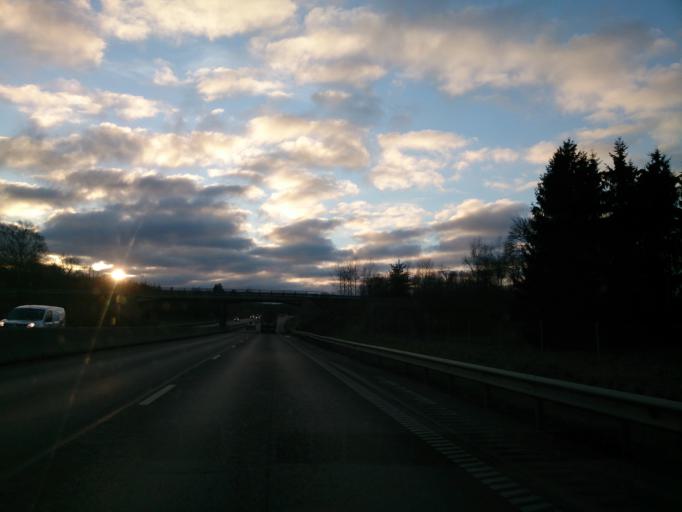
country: SE
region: OEstergoetland
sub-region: Norrkopings Kommun
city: Kimstad
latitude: 58.5256
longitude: 16.0120
